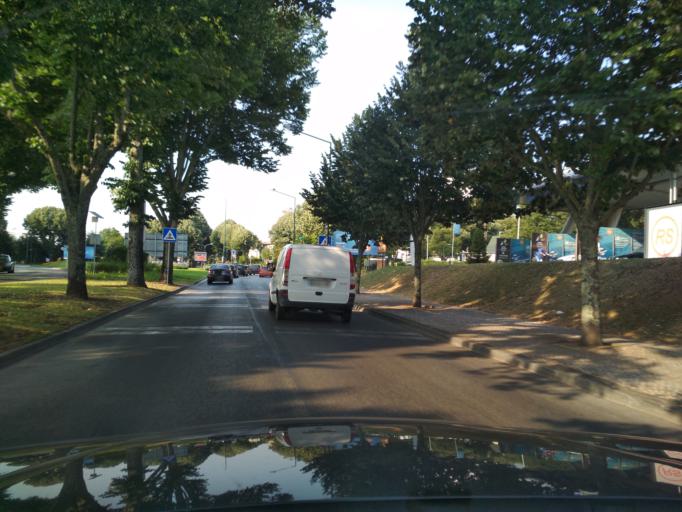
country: PT
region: Viseu
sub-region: Viseu
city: Viseu
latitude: 40.6486
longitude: -7.9199
